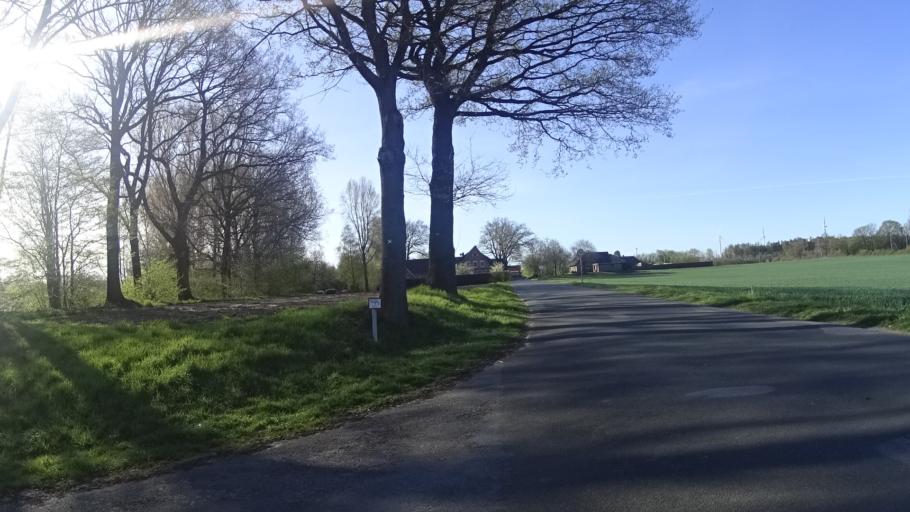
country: DE
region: North Rhine-Westphalia
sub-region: Regierungsbezirk Munster
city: Greven
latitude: 52.0715
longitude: 7.6086
